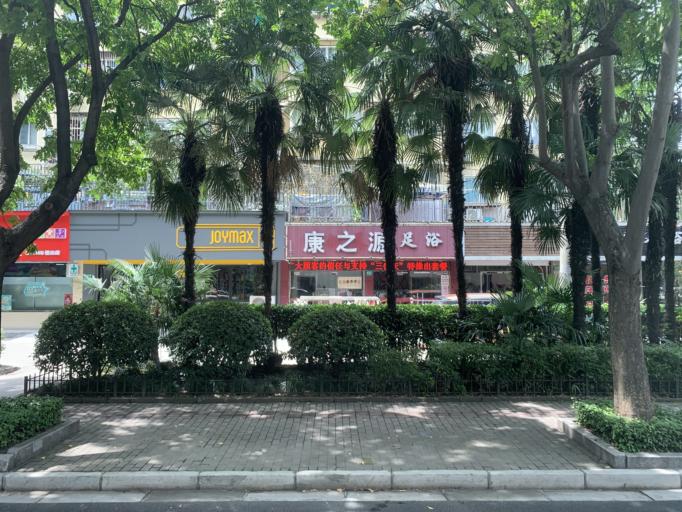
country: CN
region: Shanghai Shi
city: Huamu
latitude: 31.2490
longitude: 121.5807
